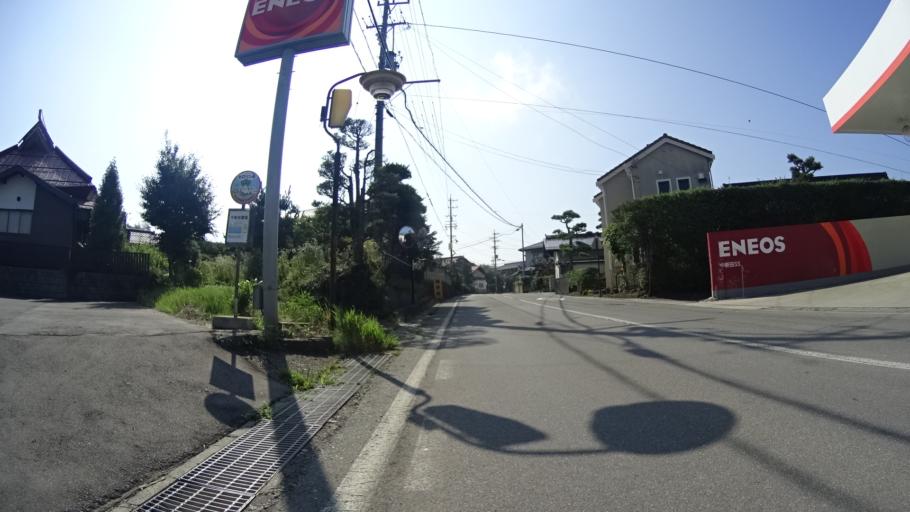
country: JP
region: Nagano
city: Chino
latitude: 35.9545
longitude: 138.2376
